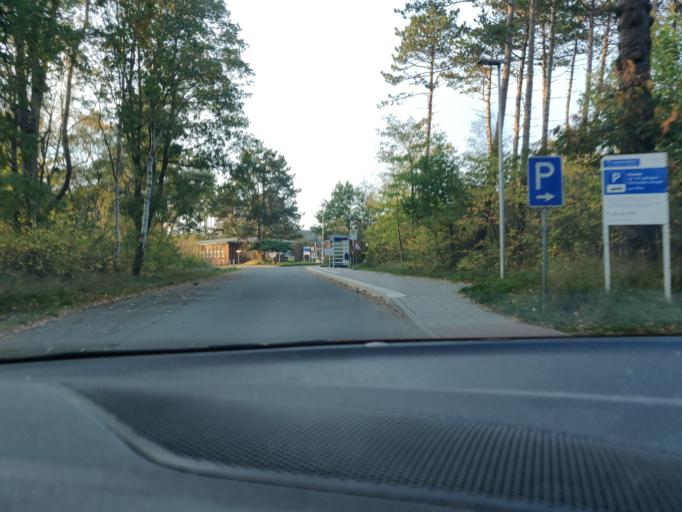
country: DE
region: Lower Saxony
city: Nordholz
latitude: 53.8640
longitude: 8.6015
